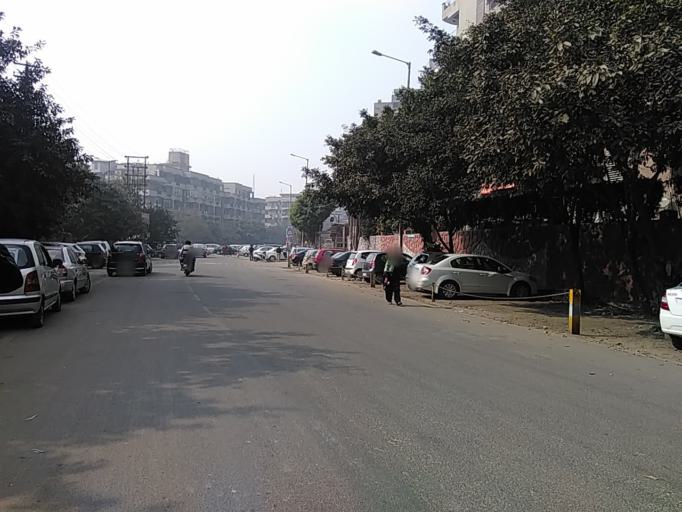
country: IN
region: Uttar Pradesh
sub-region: Gautam Buddha Nagar
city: Noida
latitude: 28.6347
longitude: 77.3650
